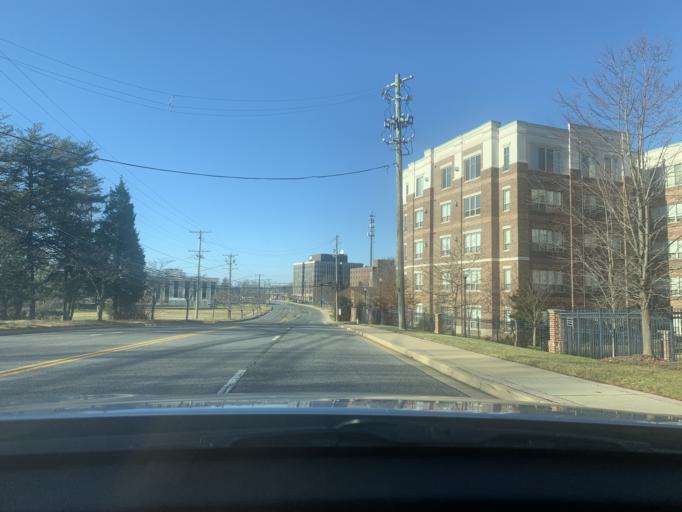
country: US
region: Maryland
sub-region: Prince George's County
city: Camp Springs
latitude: 38.8236
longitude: -76.9134
